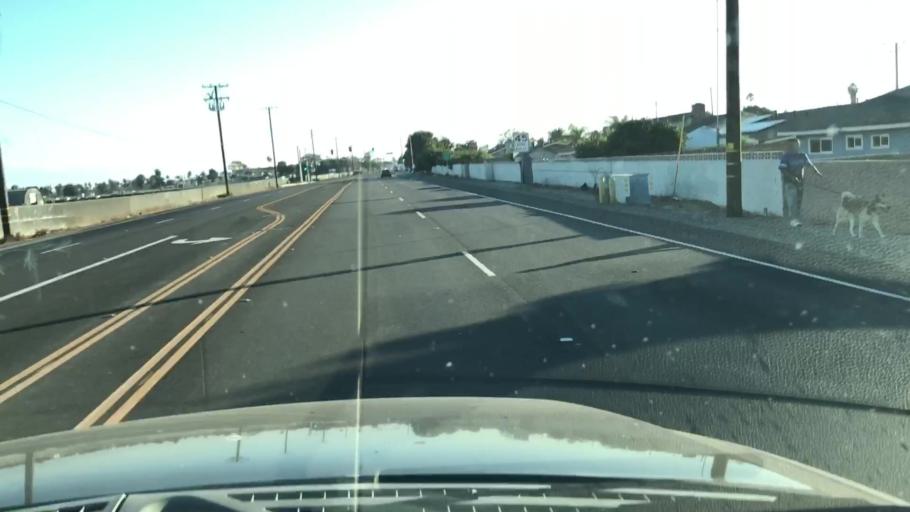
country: US
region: California
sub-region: Ventura County
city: El Rio
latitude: 34.2387
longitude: -119.1524
